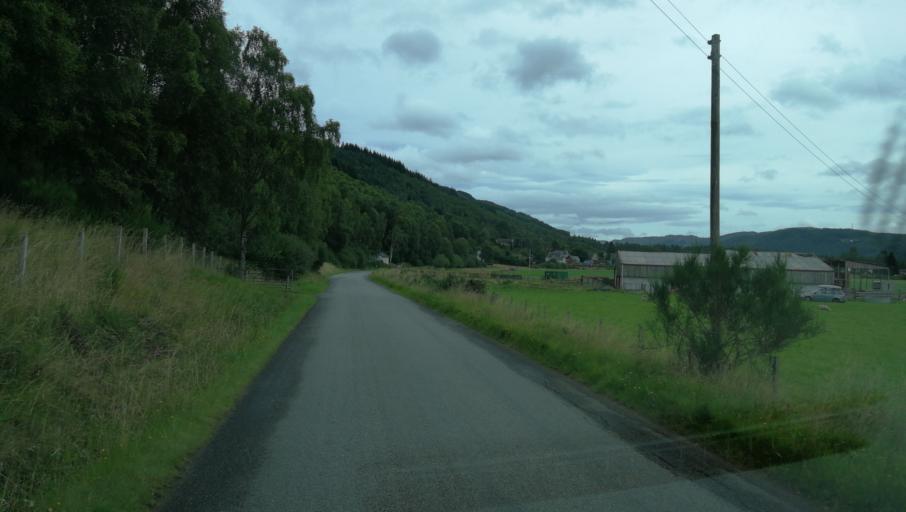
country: GB
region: Scotland
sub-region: Highland
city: Beauly
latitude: 57.3418
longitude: -4.7744
